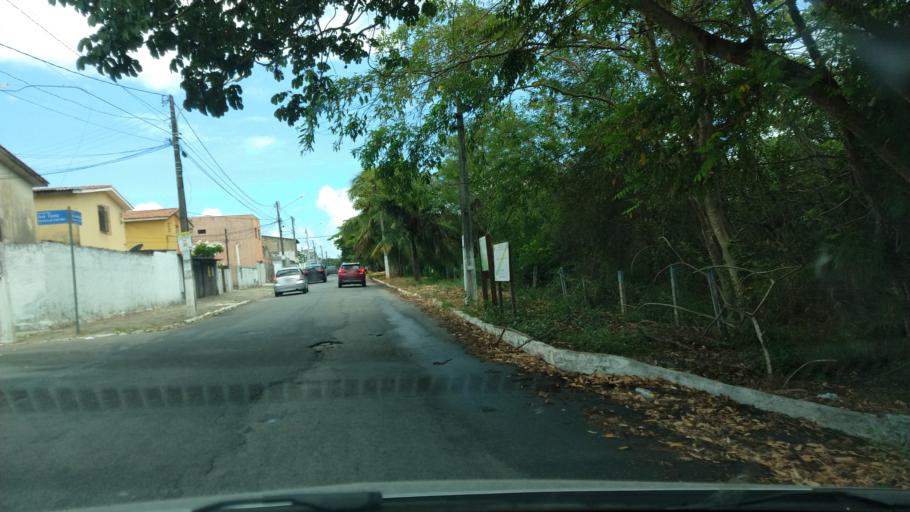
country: BR
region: Rio Grande do Norte
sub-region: Natal
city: Natal
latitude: -5.8532
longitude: -35.1996
